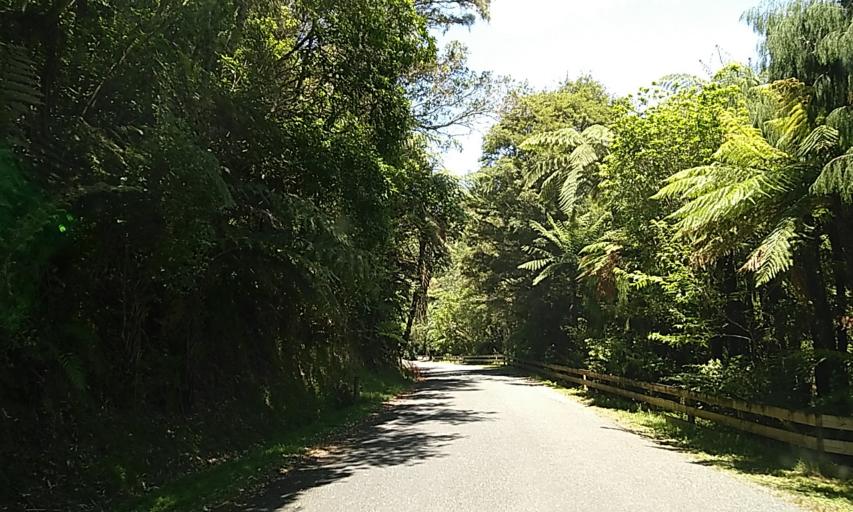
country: NZ
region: Bay of Plenty
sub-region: Tauranga City
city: Tauranga
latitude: -37.8127
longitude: 176.0462
